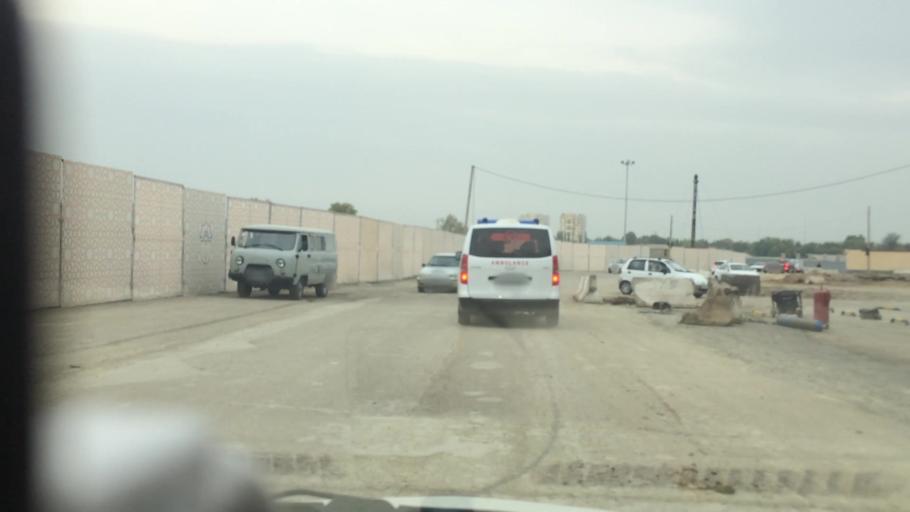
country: UZ
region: Toshkent
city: Salor
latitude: 41.3069
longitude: 69.3383
